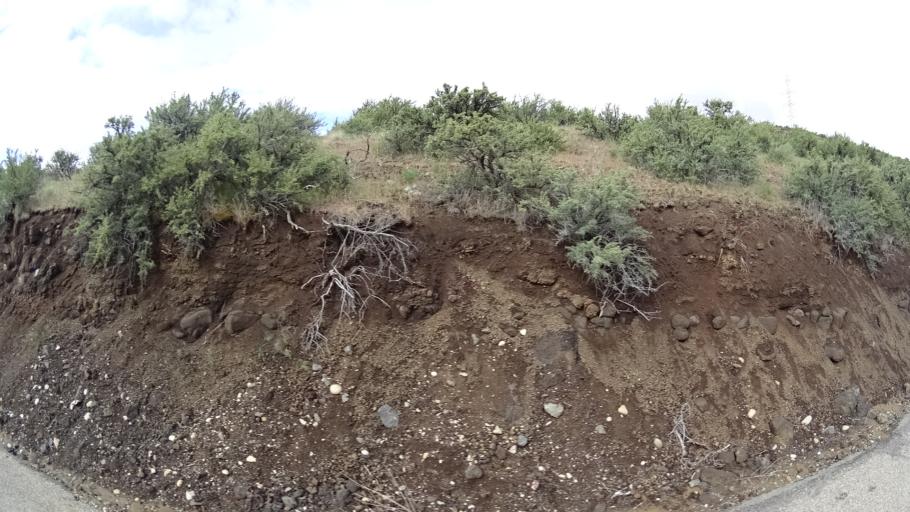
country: US
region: Idaho
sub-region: Ada County
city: Garden City
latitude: 43.7301
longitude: -116.2312
